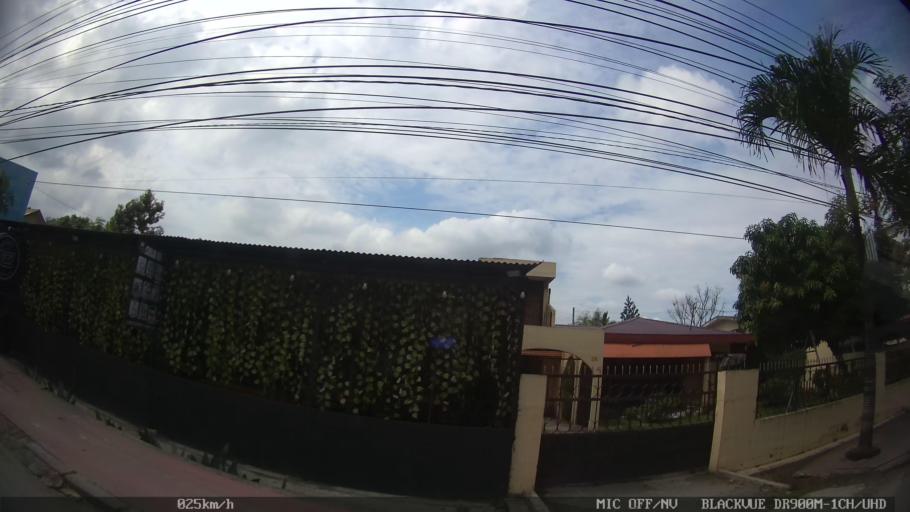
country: ID
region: North Sumatra
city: Sunggal
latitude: 3.6052
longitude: 98.6294
